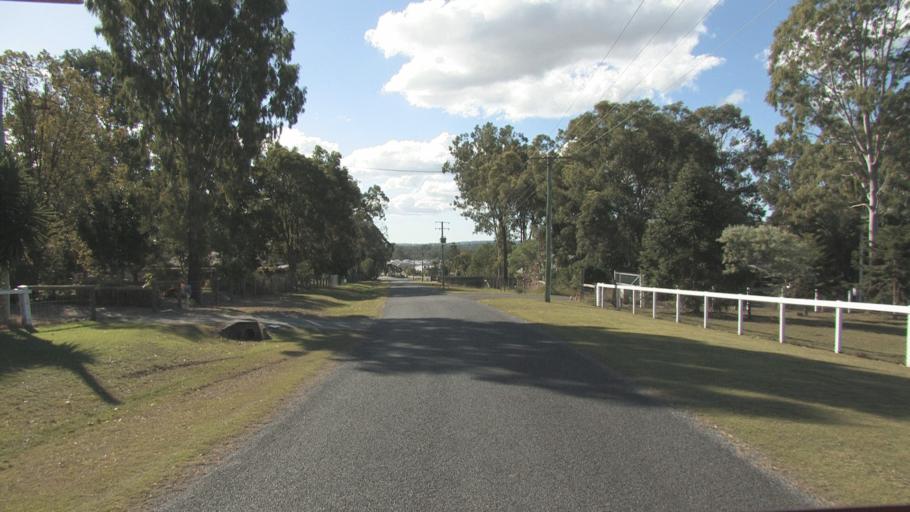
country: AU
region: Queensland
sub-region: Logan
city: Logan Reserve
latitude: -27.7158
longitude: 153.1110
